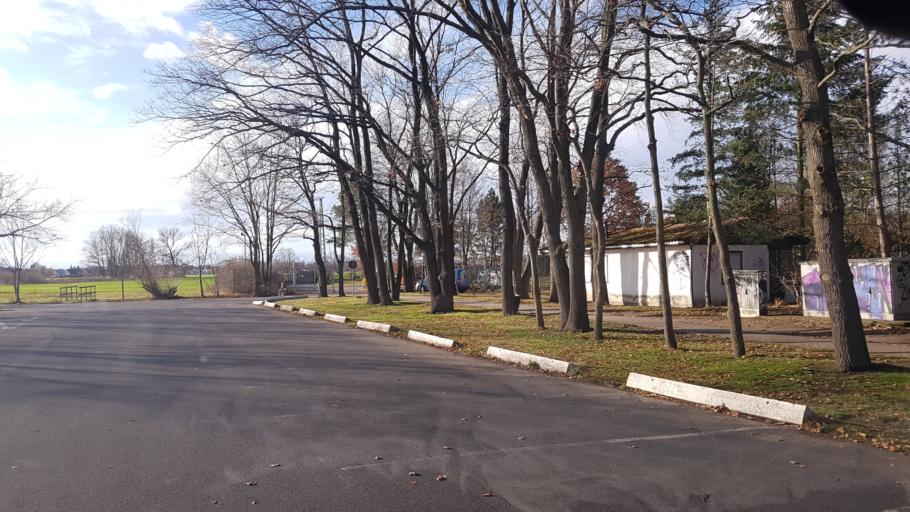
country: DE
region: Brandenburg
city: Falkenberg
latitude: 51.5943
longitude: 13.2597
